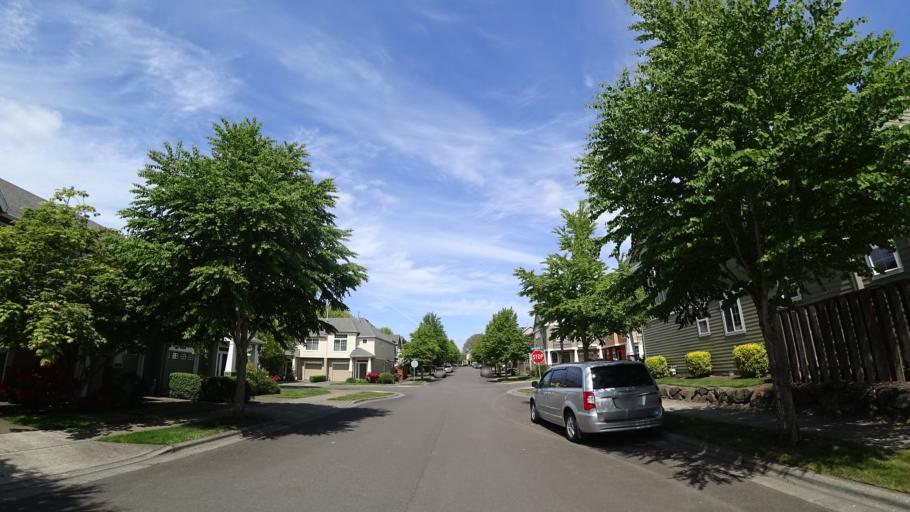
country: US
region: Oregon
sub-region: Washington County
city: Aloha
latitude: 45.4735
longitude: -122.8930
